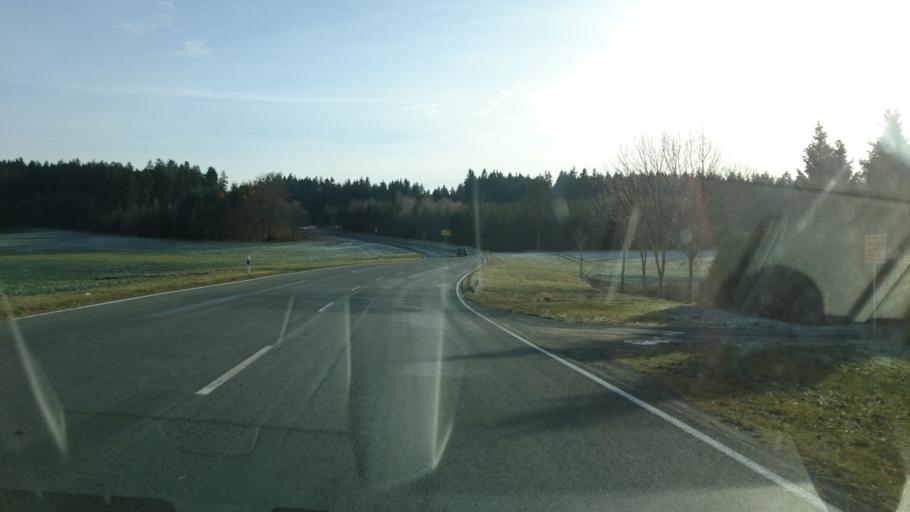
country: DE
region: Thuringia
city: Schleiz
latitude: 50.5539
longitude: 11.8306
